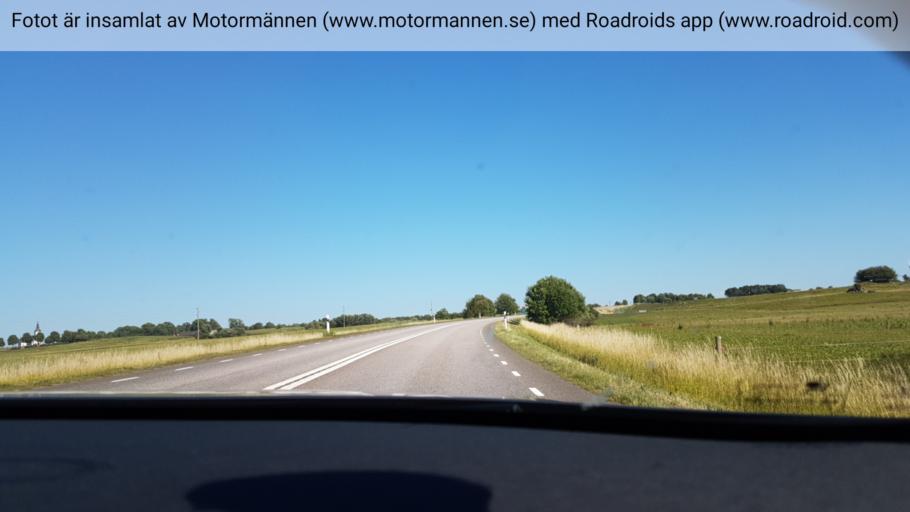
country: SE
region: Vaestra Goetaland
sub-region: Falkopings Kommun
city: Falkoeping
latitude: 58.2395
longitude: 13.5396
